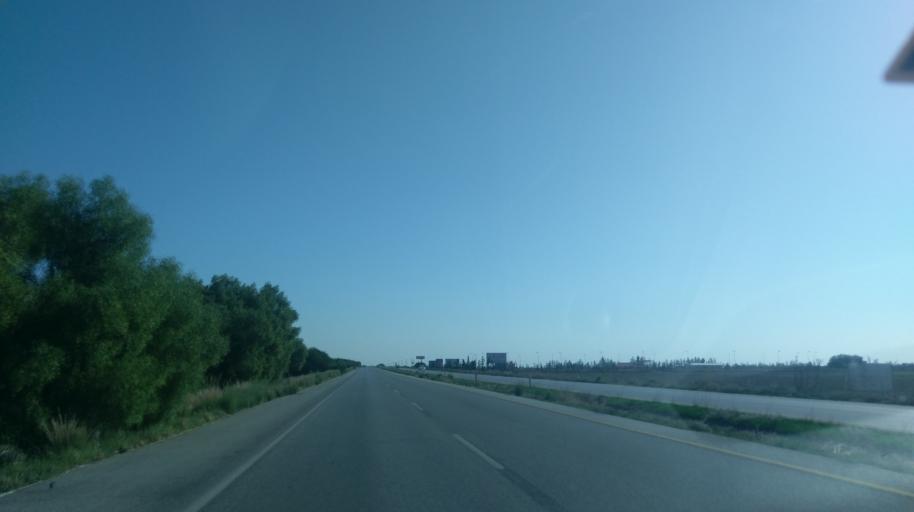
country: CY
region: Ammochostos
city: Lefkonoiko
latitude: 35.1845
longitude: 33.6784
